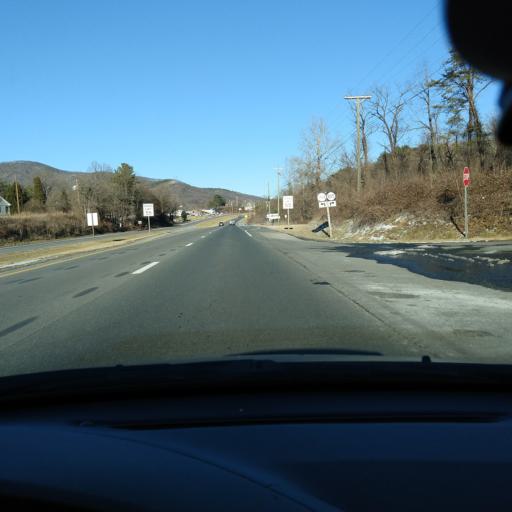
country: US
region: Virginia
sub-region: Botetourt County
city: Blue Ridge
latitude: 37.3806
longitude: -79.8043
